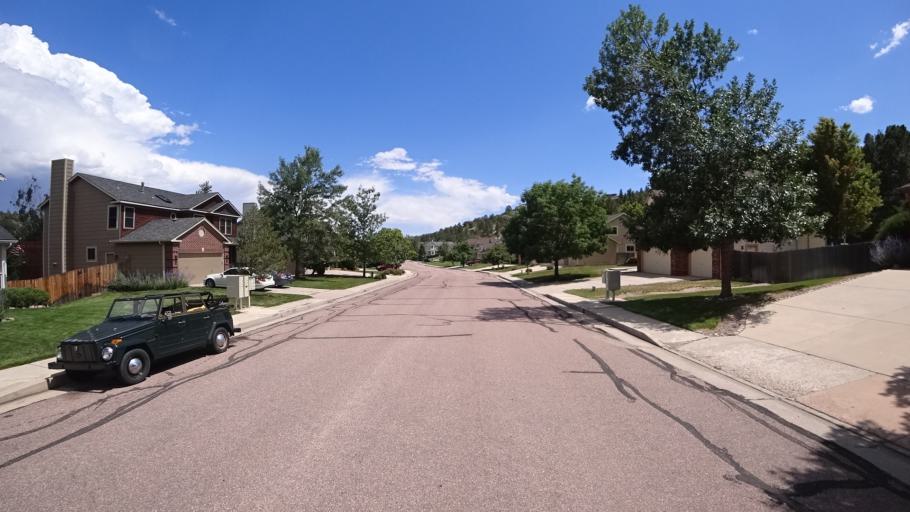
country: US
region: Colorado
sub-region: El Paso County
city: Air Force Academy
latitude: 38.9418
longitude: -104.8485
